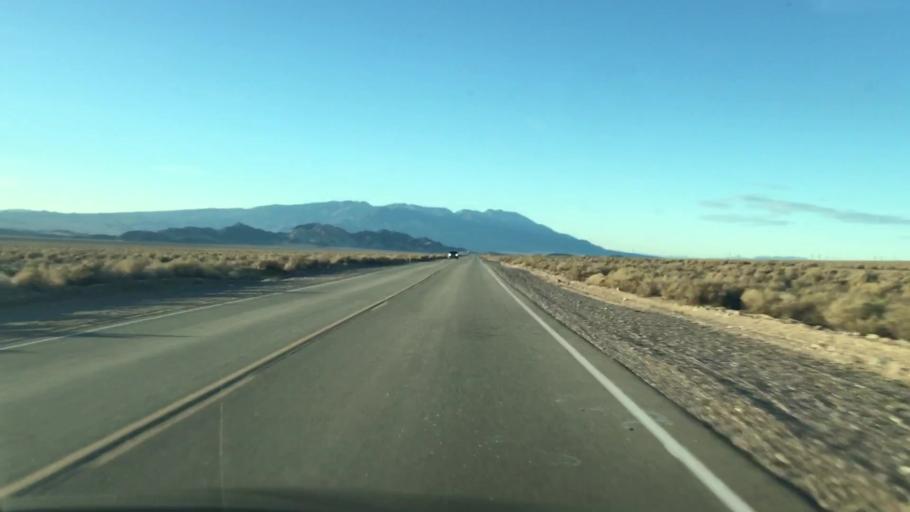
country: US
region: California
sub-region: San Bernardino County
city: Fort Irwin
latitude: 35.3482
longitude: -116.0875
